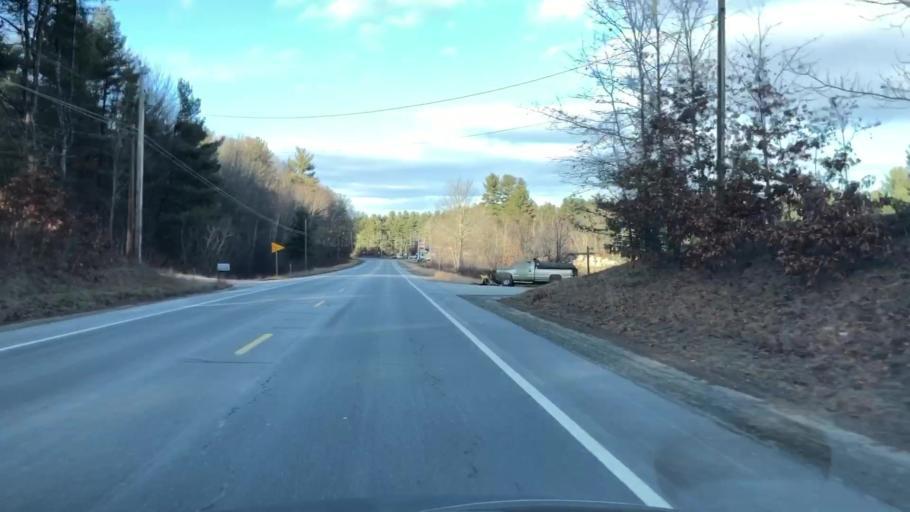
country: US
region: New Hampshire
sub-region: Hillsborough County
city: Brookline
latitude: 42.7200
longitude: -71.6624
